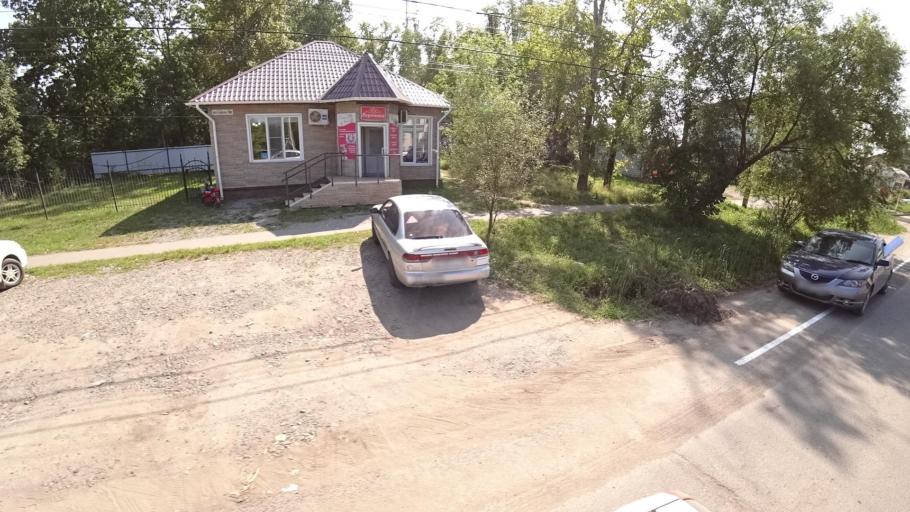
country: RU
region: Khabarovsk Krai
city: Khor
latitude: 47.9649
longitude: 135.0562
